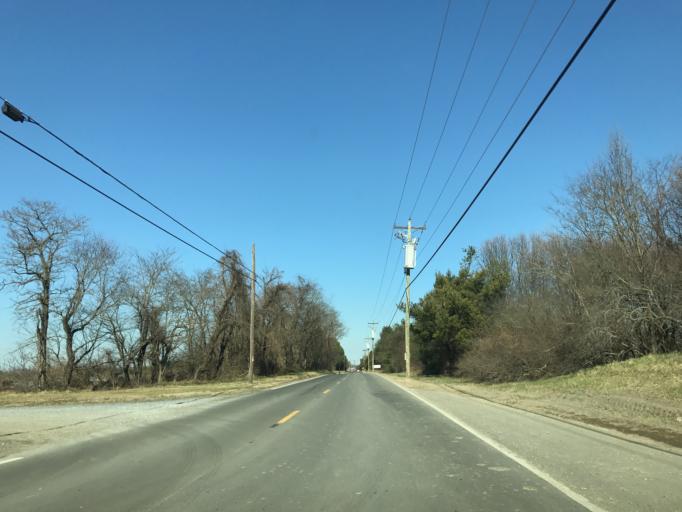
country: US
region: Maryland
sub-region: Queen Anne's County
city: Centreville
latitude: 39.0031
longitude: -76.1349
